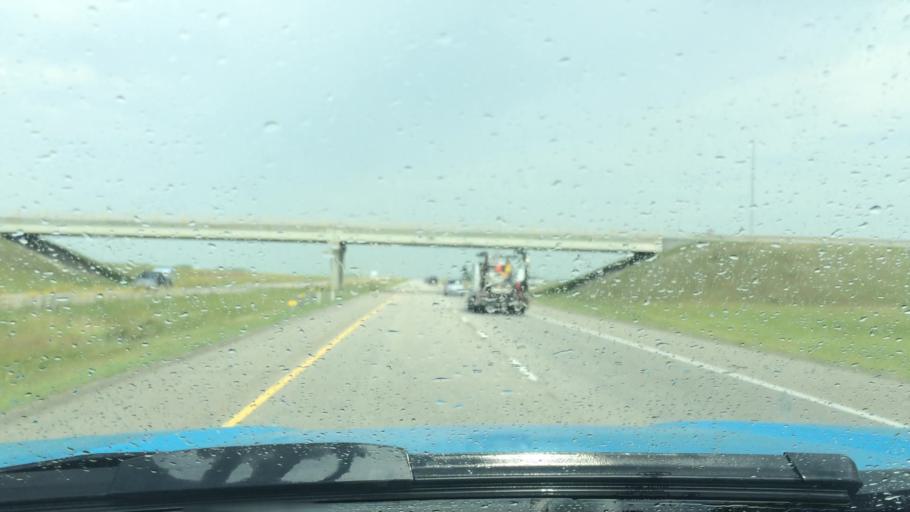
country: CA
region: Alberta
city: Didsbury
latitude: 51.6631
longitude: -114.0254
